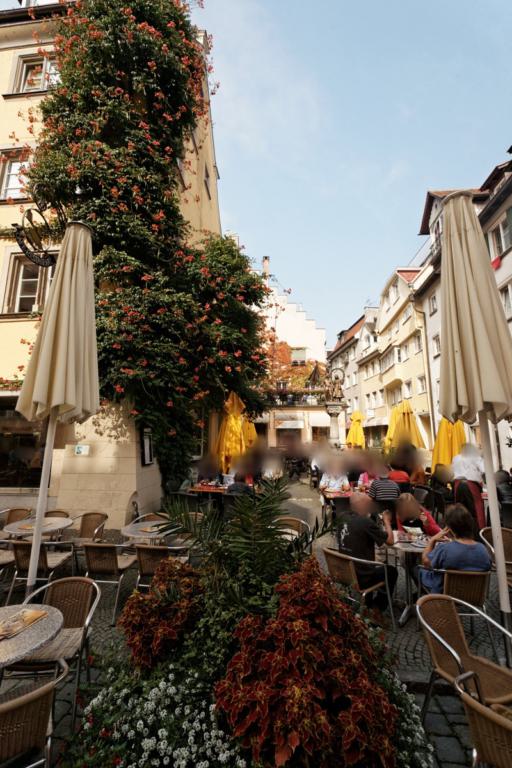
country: DE
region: Bavaria
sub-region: Swabia
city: Lindau
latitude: 47.5465
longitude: 9.6846
